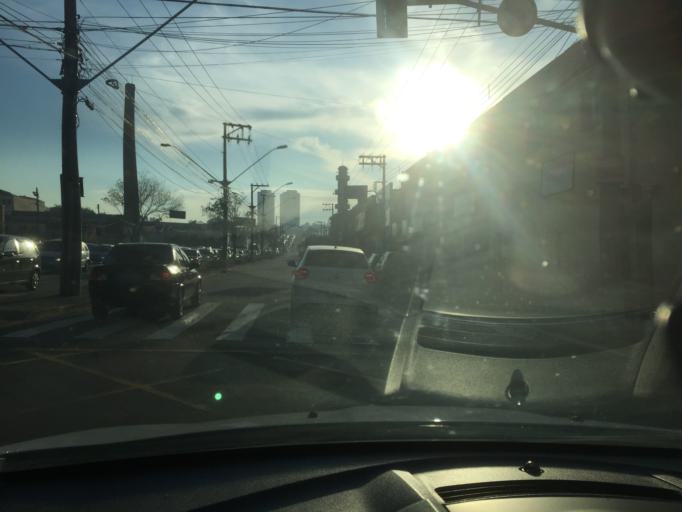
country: BR
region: Sao Paulo
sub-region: Jundiai
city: Jundiai
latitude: -23.1938
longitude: -46.8778
